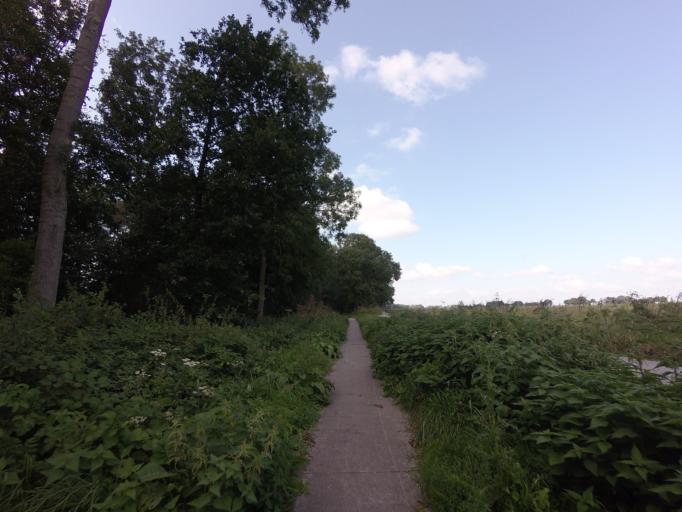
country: NL
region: Flevoland
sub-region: Gemeente Noordoostpolder
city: Ens
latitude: 52.6251
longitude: 5.7692
